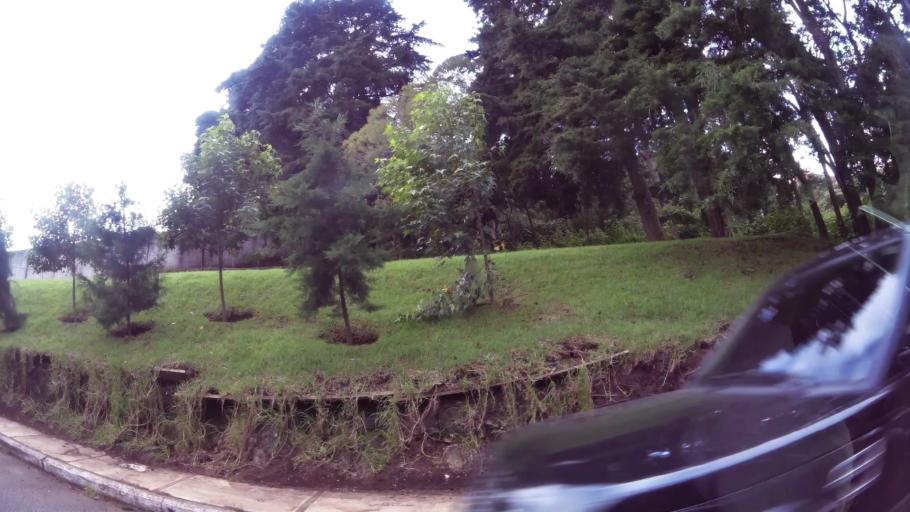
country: GT
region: Guatemala
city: San Jose Pinula
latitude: 14.5412
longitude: -90.4560
